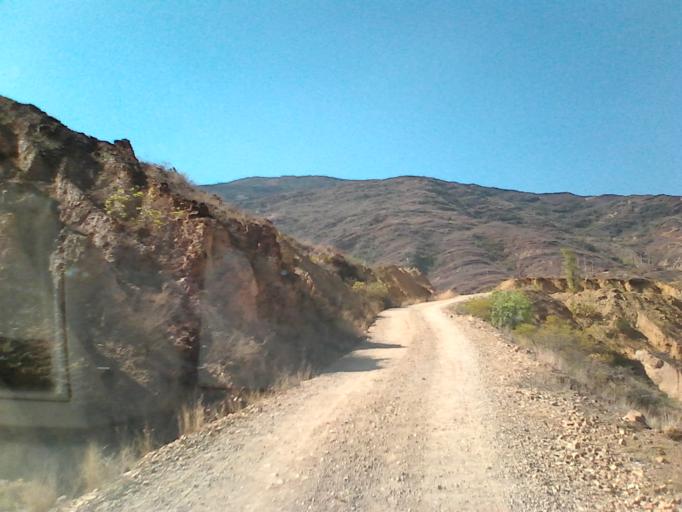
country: CO
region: Boyaca
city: Sachica
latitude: 5.5589
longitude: -73.5491
